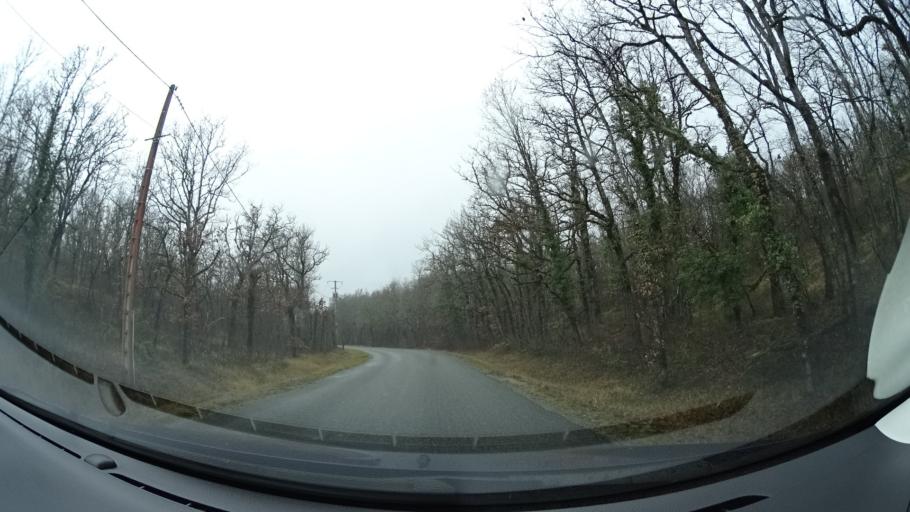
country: FR
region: Midi-Pyrenees
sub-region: Departement du Lot
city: Montcuq
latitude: 44.3863
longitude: 1.2248
